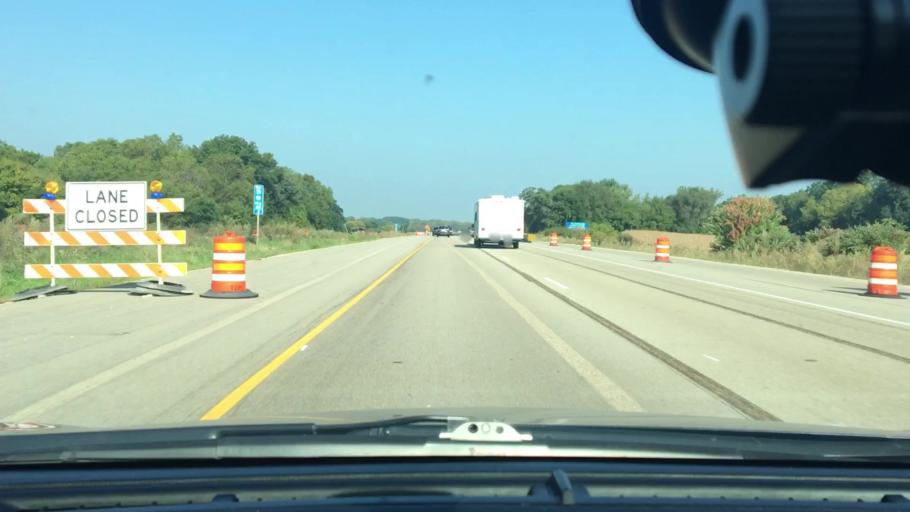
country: US
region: Wisconsin
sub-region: Rock County
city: Edgerton
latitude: 42.8058
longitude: -89.0099
